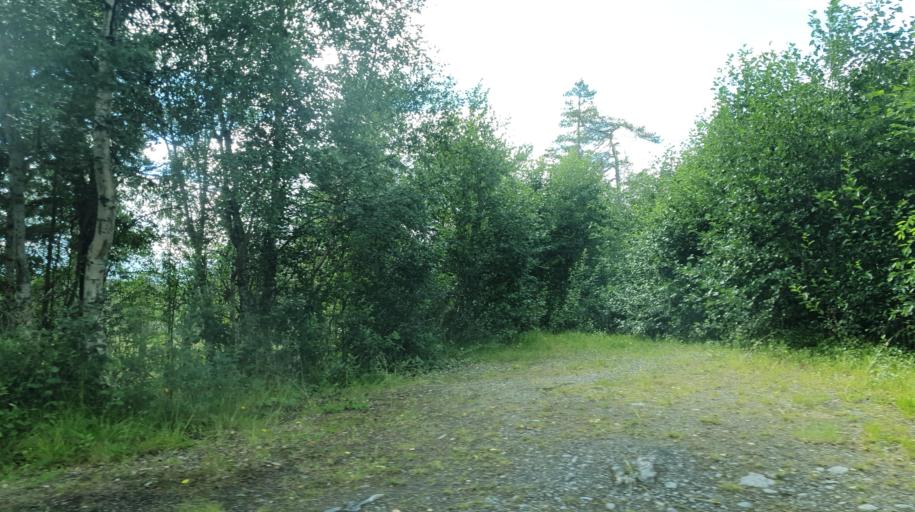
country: NO
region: Nord-Trondelag
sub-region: Levanger
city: Skogn
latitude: 63.5834
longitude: 11.2450
